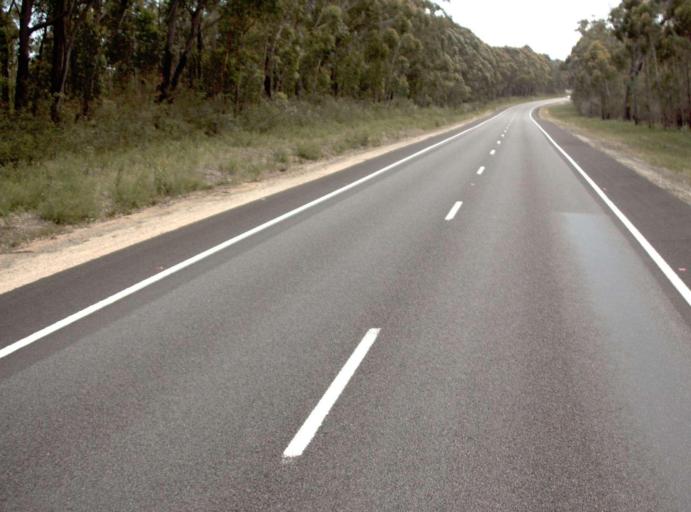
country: AU
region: New South Wales
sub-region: Bega Valley
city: Eden
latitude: -37.5129
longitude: 149.5102
